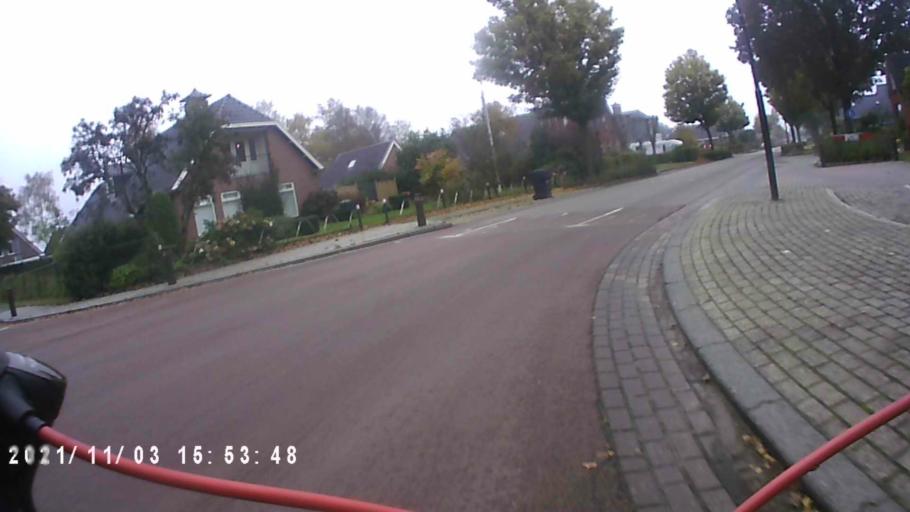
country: NL
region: Groningen
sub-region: Gemeente Leek
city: Leek
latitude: 53.0703
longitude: 6.3321
